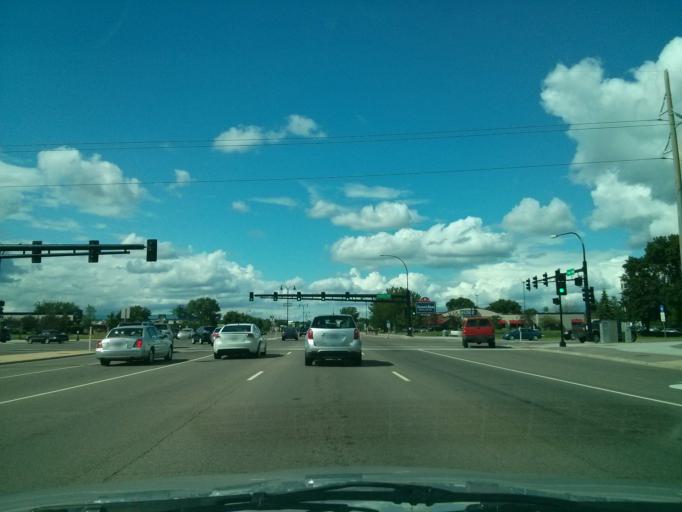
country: US
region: Minnesota
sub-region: Dakota County
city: Apple Valley
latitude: 44.7313
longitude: -93.2176
